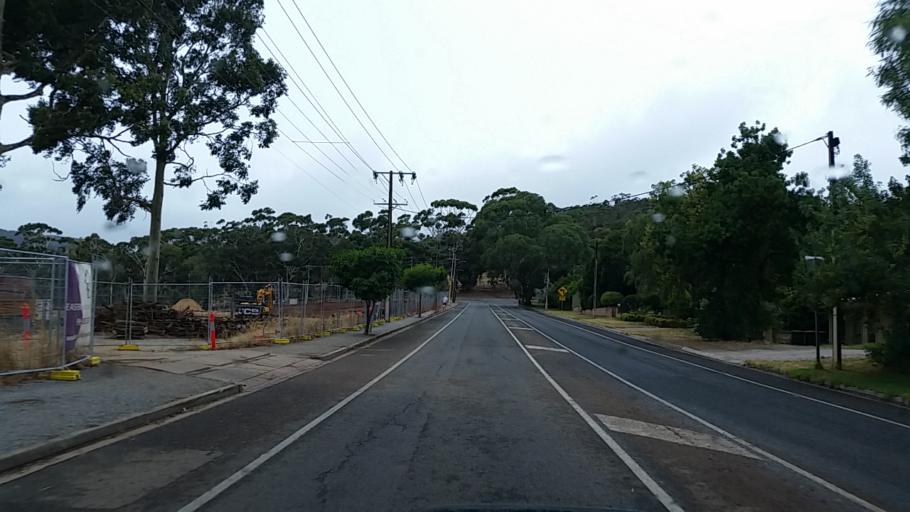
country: AU
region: South Australia
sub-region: Adelaide Hills
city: Adelaide Hills
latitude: -34.9002
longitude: 138.6890
